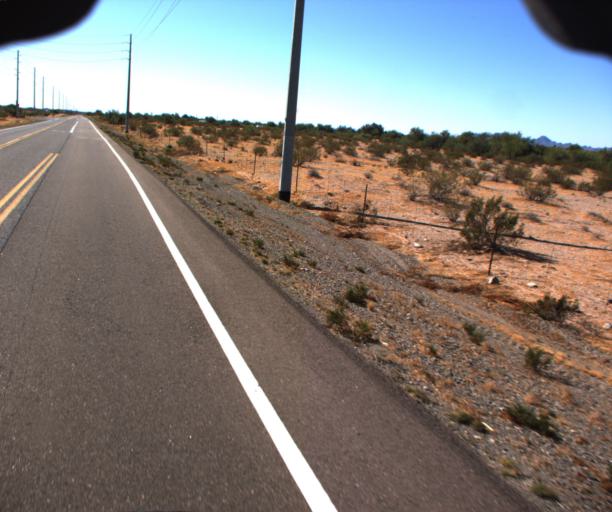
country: US
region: Arizona
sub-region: La Paz County
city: Cienega Springs
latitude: 33.9620
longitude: -114.0332
